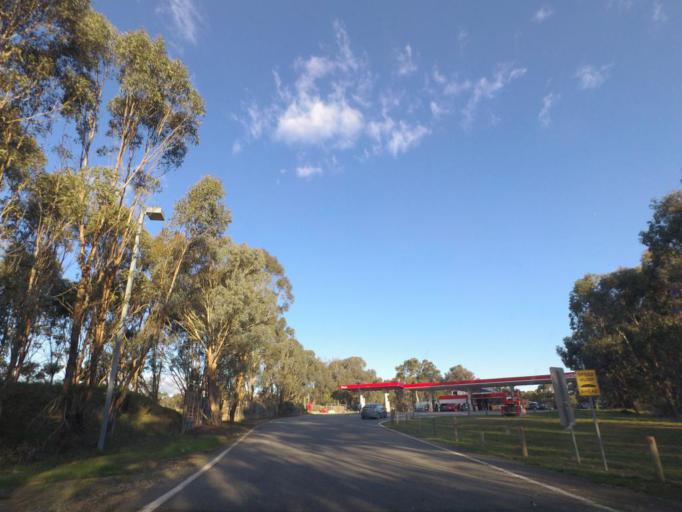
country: AU
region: Victoria
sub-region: Murrindindi
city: Kinglake West
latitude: -37.0624
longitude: 145.1017
